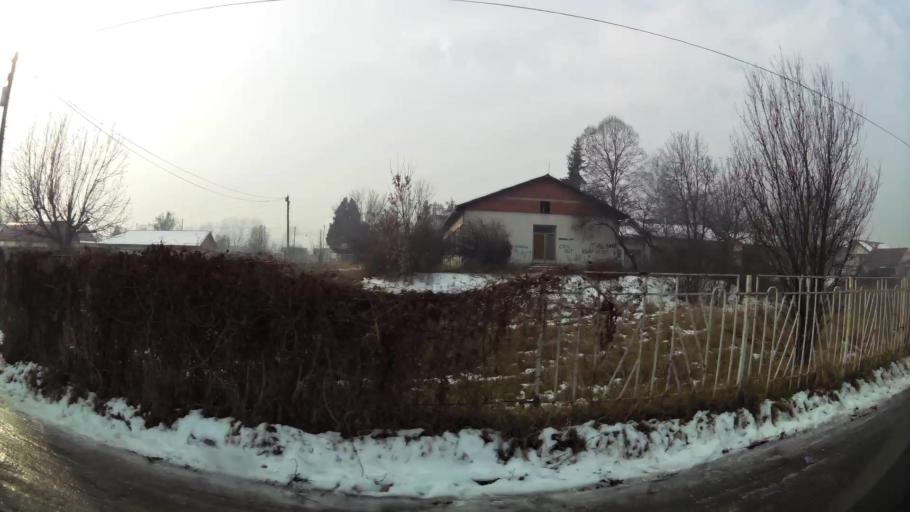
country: MK
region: Ilinden
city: Jurumleri
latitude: 41.9778
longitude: 21.5309
